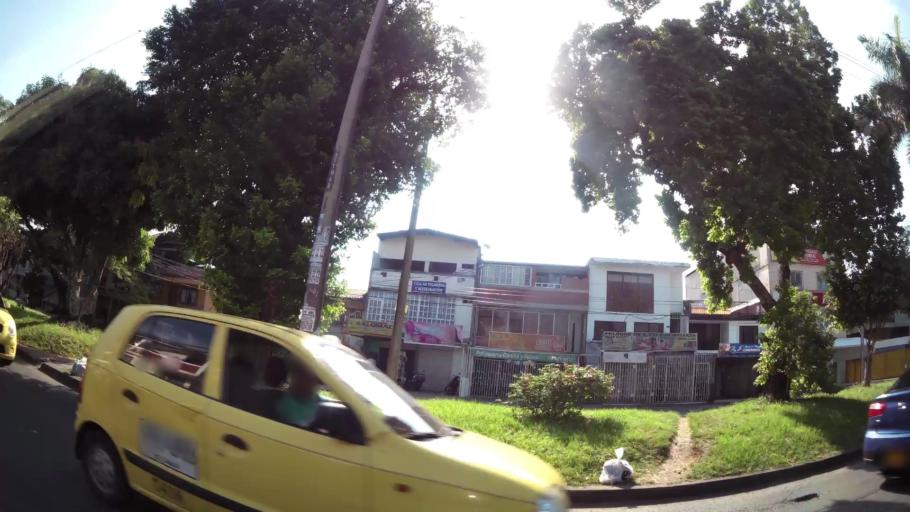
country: CO
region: Valle del Cauca
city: Cali
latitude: 3.4163
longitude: -76.5279
